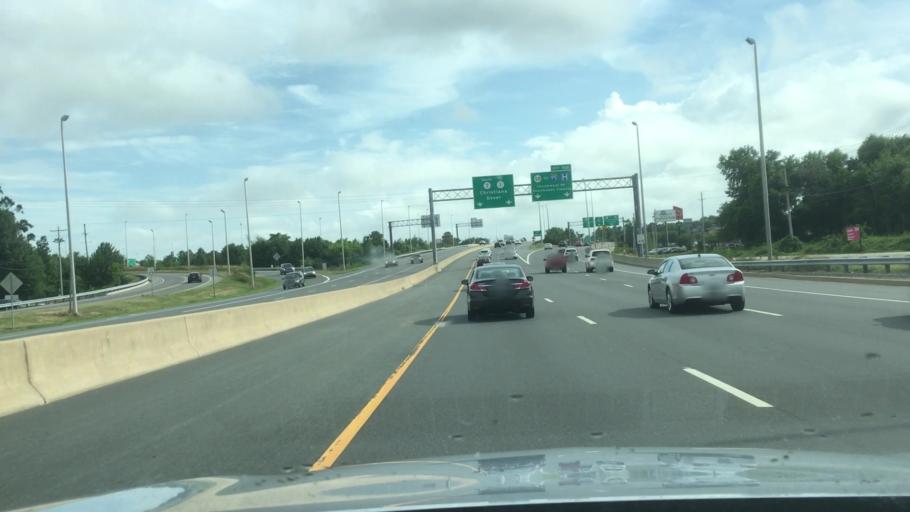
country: US
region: Delaware
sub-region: New Castle County
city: Newport
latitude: 39.6924
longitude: -75.6532
